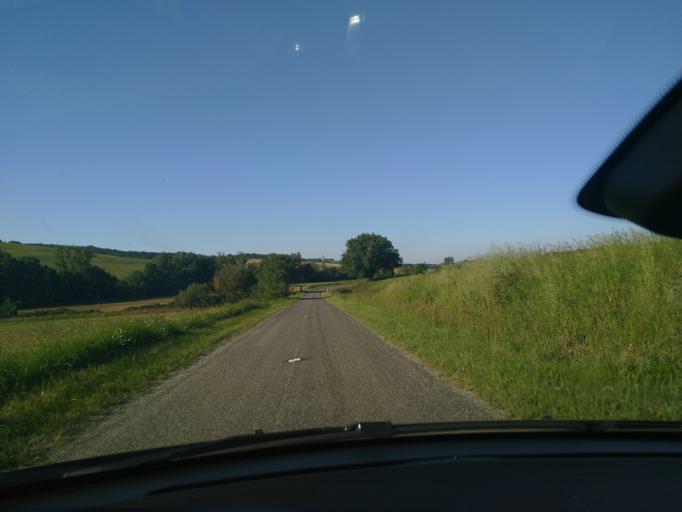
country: FR
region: Midi-Pyrenees
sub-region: Departement du Tarn-et-Garonne
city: Beaumont-de-Lomagne
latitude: 43.8259
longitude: 1.0567
